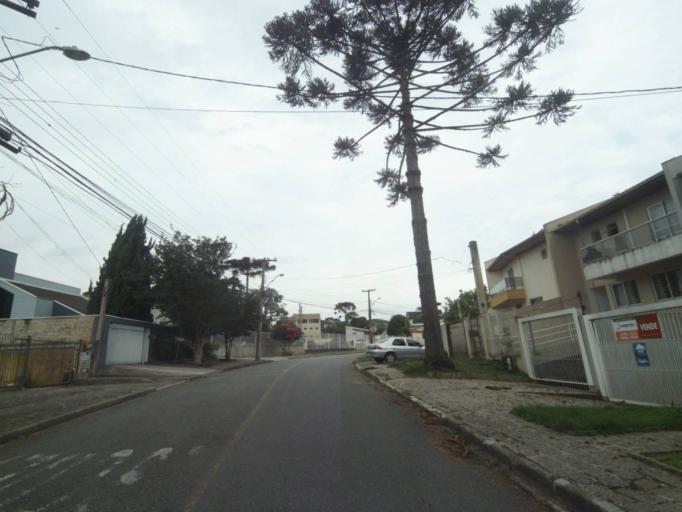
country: BR
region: Parana
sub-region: Curitiba
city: Curitiba
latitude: -25.4104
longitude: -49.2986
